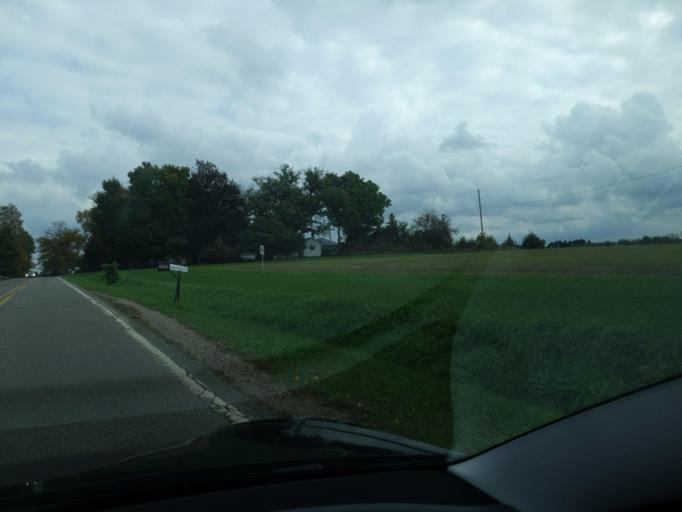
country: US
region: Michigan
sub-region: Ingham County
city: Leslie
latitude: 42.4113
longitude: -84.3938
